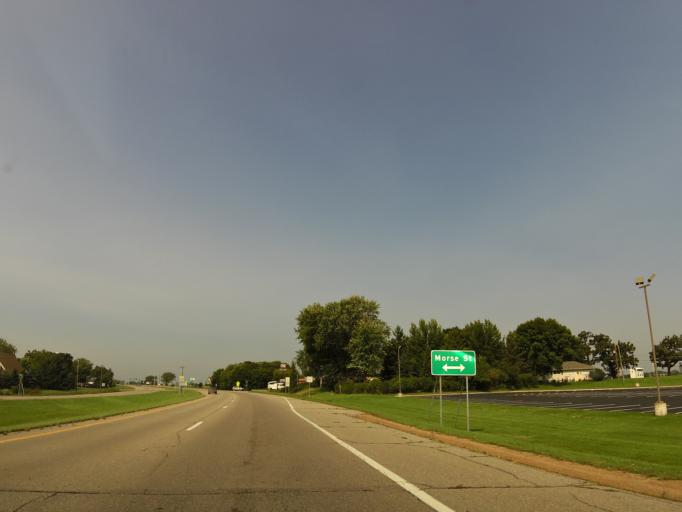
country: US
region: Minnesota
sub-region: Carver County
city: Norwood Young America
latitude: 44.7721
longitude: -93.9223
